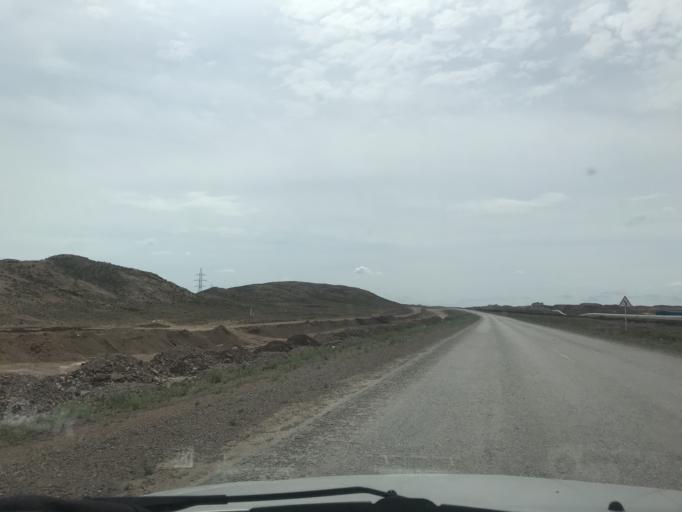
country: KZ
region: Zhambyl
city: Mynaral
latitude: 45.3733
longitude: 73.6567
